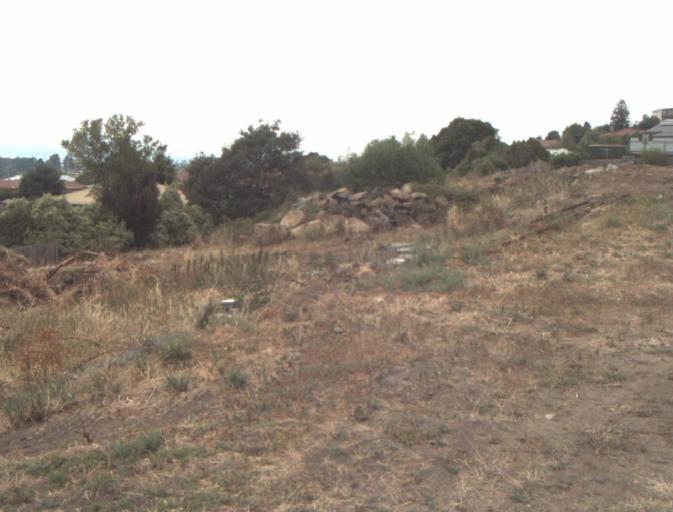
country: AU
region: Tasmania
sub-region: Launceston
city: Summerhill
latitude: -41.4677
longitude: 147.1487
